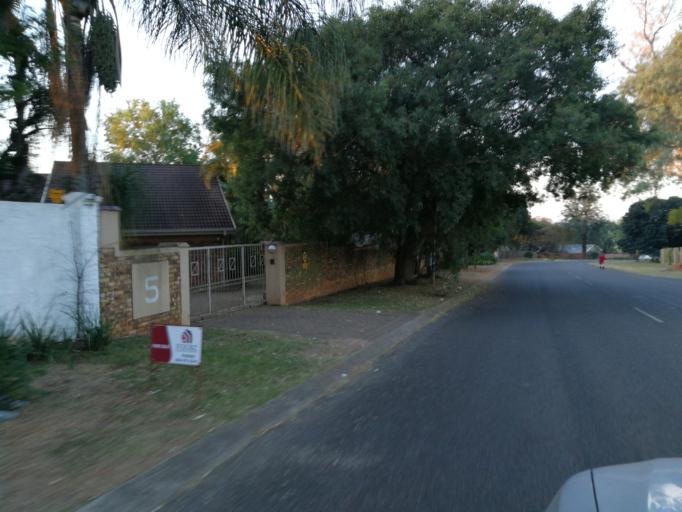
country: ZA
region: Mpumalanga
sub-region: Ehlanzeni District
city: White River
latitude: -25.3199
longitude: 31.0193
